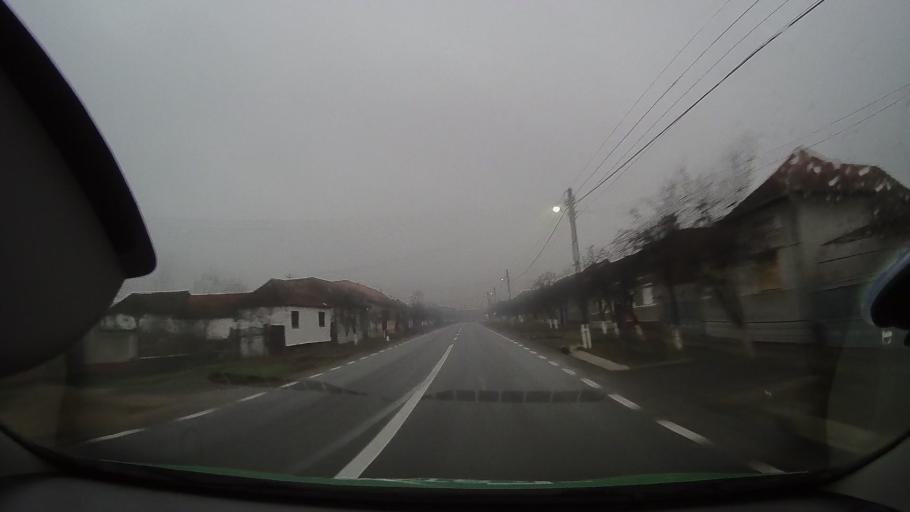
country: RO
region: Bihor
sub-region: Comuna Olcea
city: Calacea
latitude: 46.6416
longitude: 21.9554
